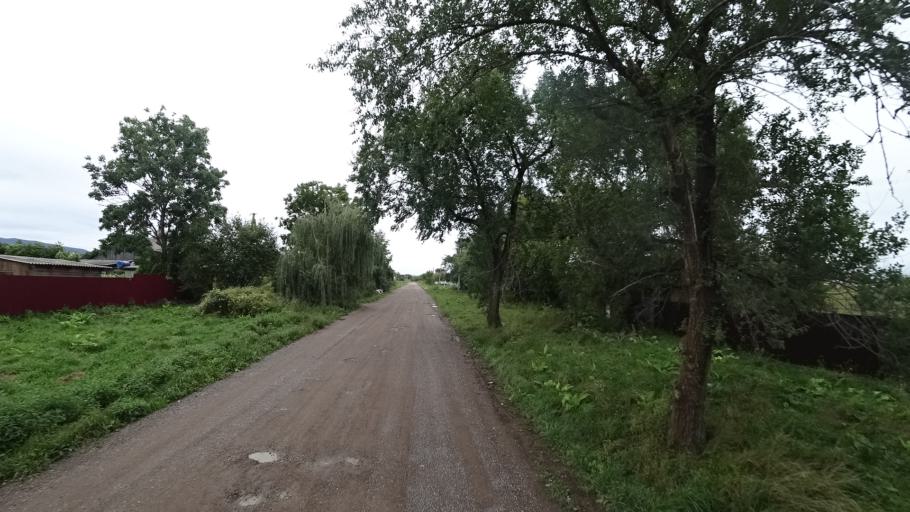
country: RU
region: Primorskiy
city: Chernigovka
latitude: 44.3398
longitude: 132.5625
